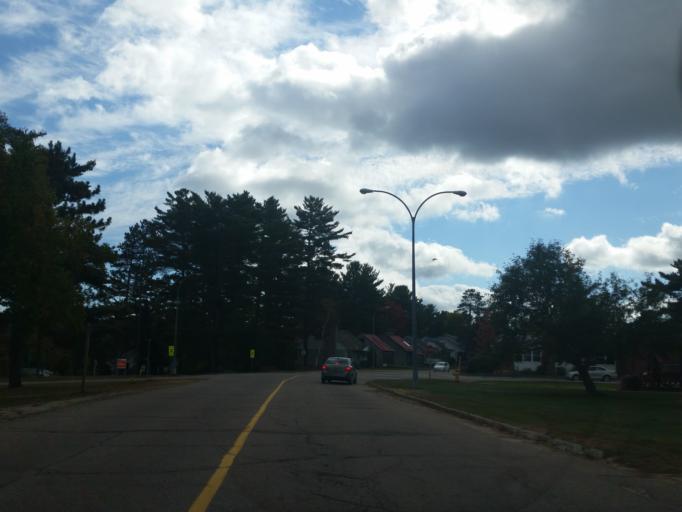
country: CA
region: Ontario
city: Deep River
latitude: 46.1017
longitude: -77.4869
